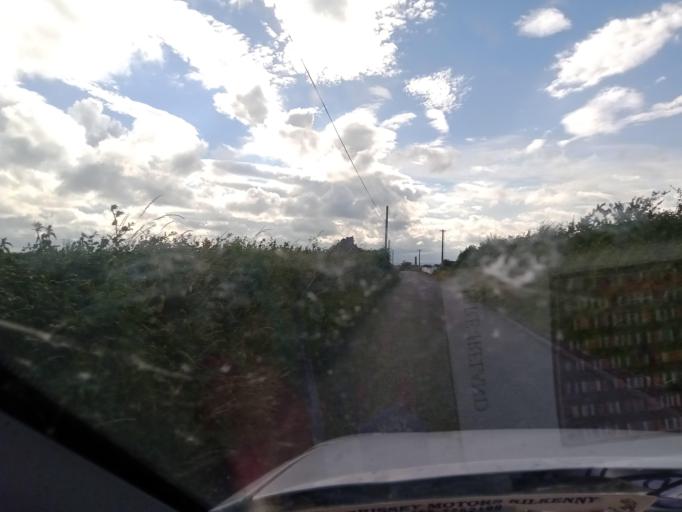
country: IE
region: Leinster
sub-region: Laois
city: Rathdowney
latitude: 52.7759
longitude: -7.5290
